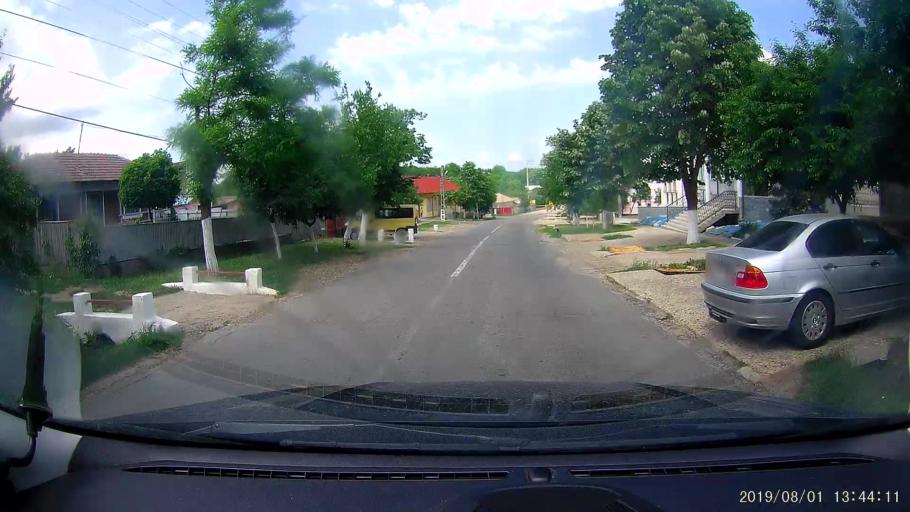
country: RO
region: Galati
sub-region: Comuna Oancea
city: Oancea
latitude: 45.9193
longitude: 28.1128
